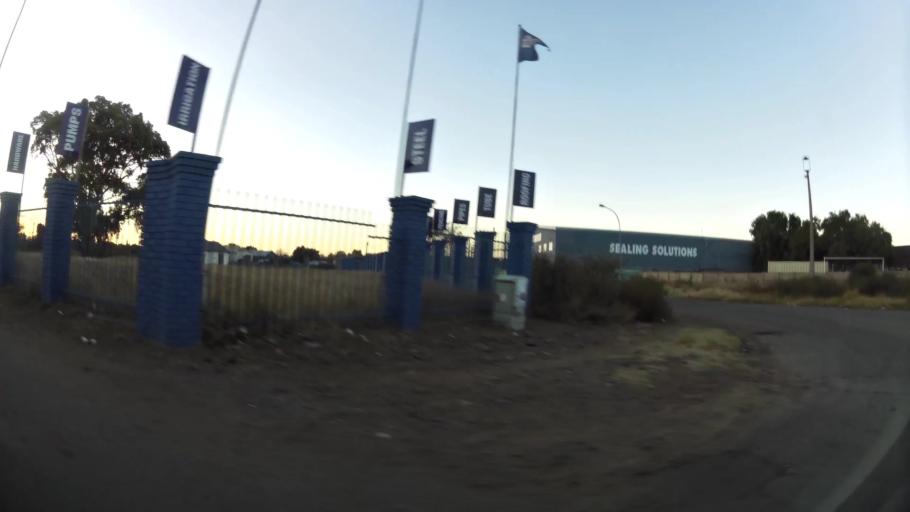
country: ZA
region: Northern Cape
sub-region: Frances Baard District Municipality
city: Kimberley
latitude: -28.7294
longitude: 24.7704
